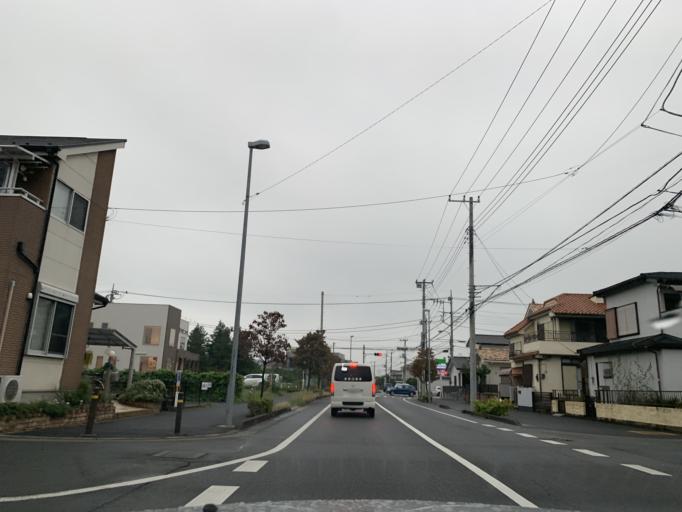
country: JP
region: Chiba
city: Nagareyama
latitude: 35.9019
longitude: 139.9180
